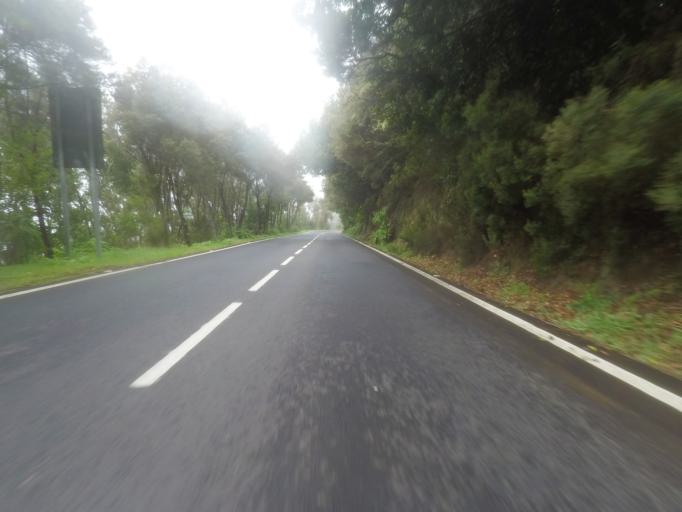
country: ES
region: Canary Islands
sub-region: Provincia de Santa Cruz de Tenerife
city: Alajero
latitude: 28.1186
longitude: -17.2472
